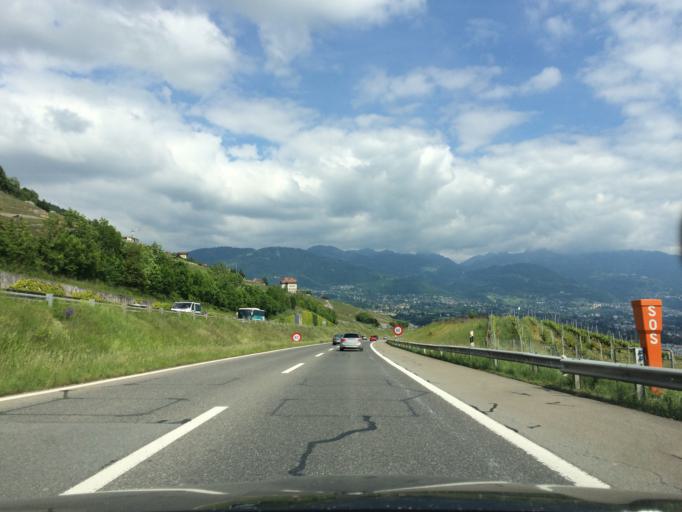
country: CH
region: Vaud
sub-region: Riviera-Pays-d'Enhaut District
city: Chardonne
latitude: 46.4751
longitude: 6.8133
